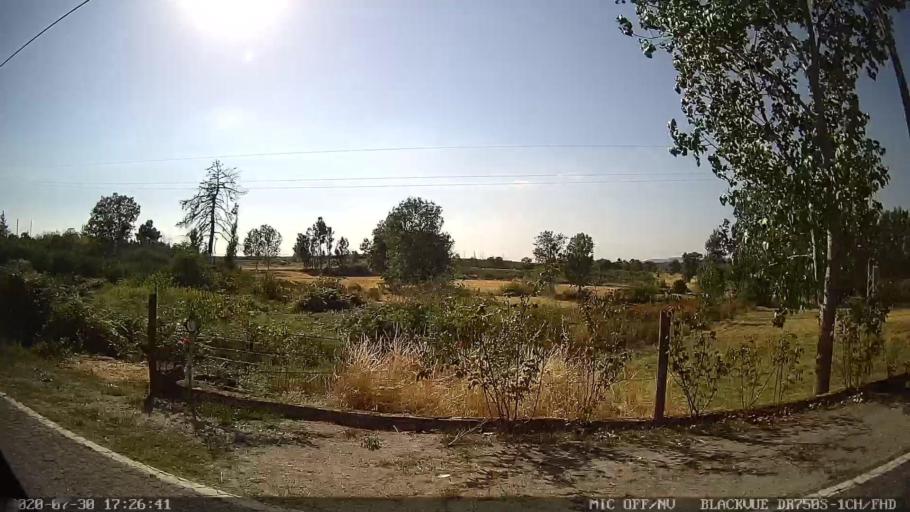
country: PT
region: Vila Real
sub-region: Murca
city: Murca
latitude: 41.3170
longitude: -7.4643
